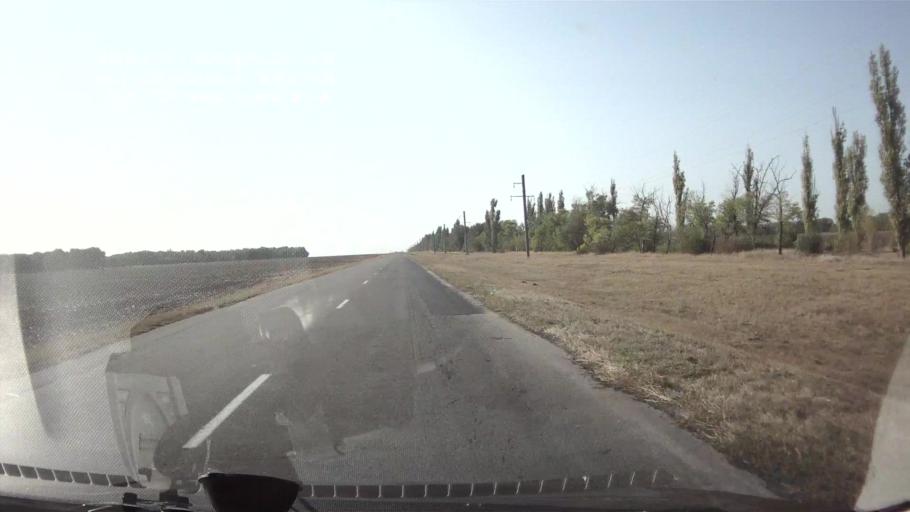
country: RU
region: Rostov
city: Tselina
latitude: 46.5304
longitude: 40.8998
